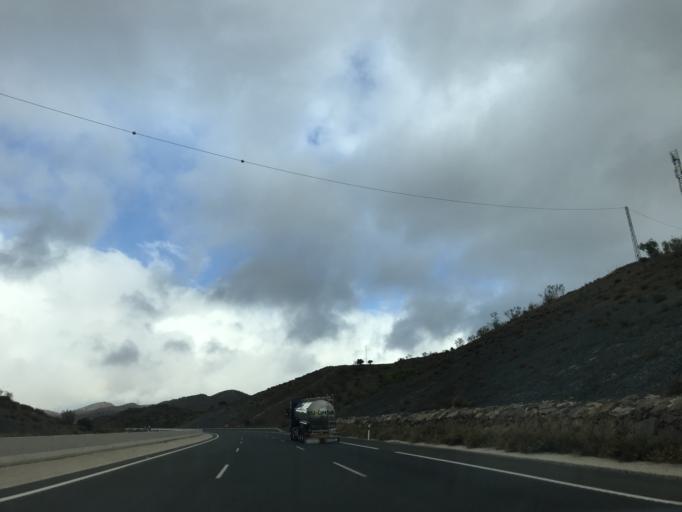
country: ES
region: Andalusia
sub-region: Provincia de Malaga
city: Almogia
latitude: 36.8118
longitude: -4.4706
